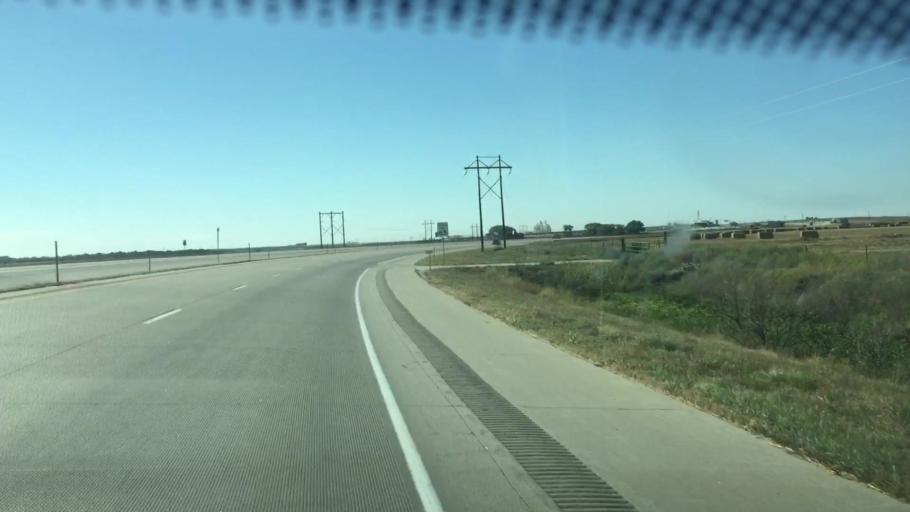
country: US
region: Colorado
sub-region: Prowers County
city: Lamar
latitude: 38.1089
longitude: -102.6955
